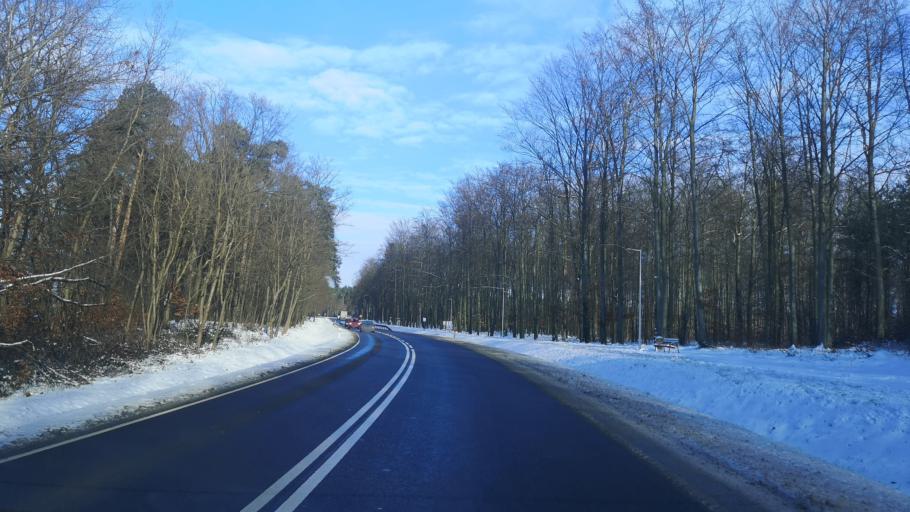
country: PL
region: Subcarpathian Voivodeship
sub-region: Powiat przeworski
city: Tryncza
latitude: 50.1233
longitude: 22.5341
